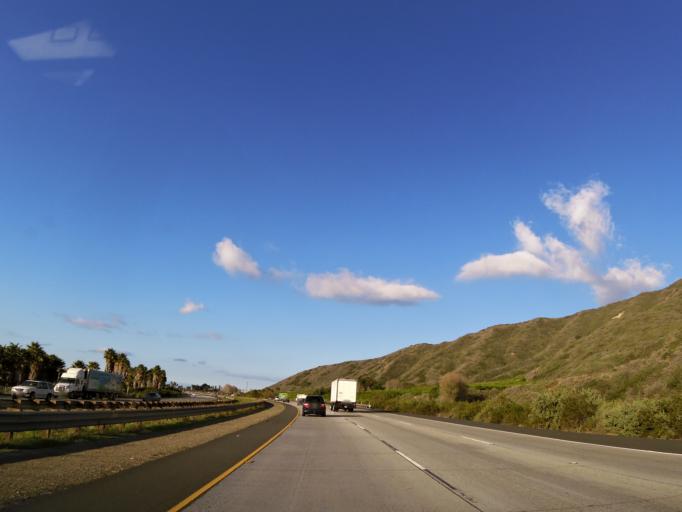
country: US
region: California
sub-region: Ventura County
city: Ventura
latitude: 34.3224
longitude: -119.3752
